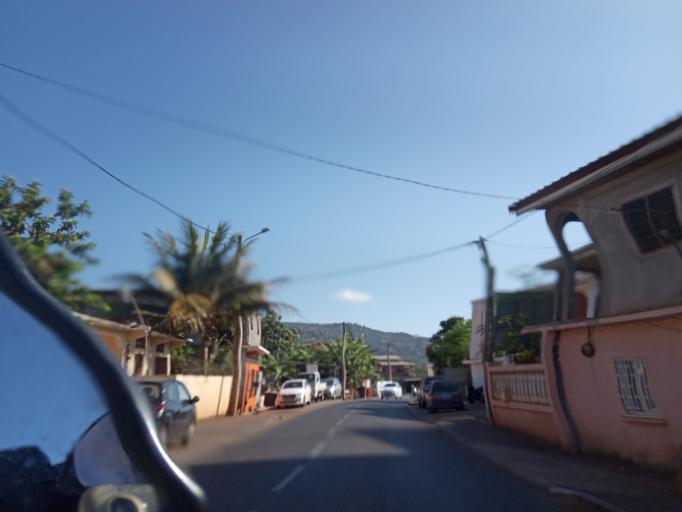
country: YT
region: Bandrele
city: Bandrele
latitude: -12.9096
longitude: 45.1928
